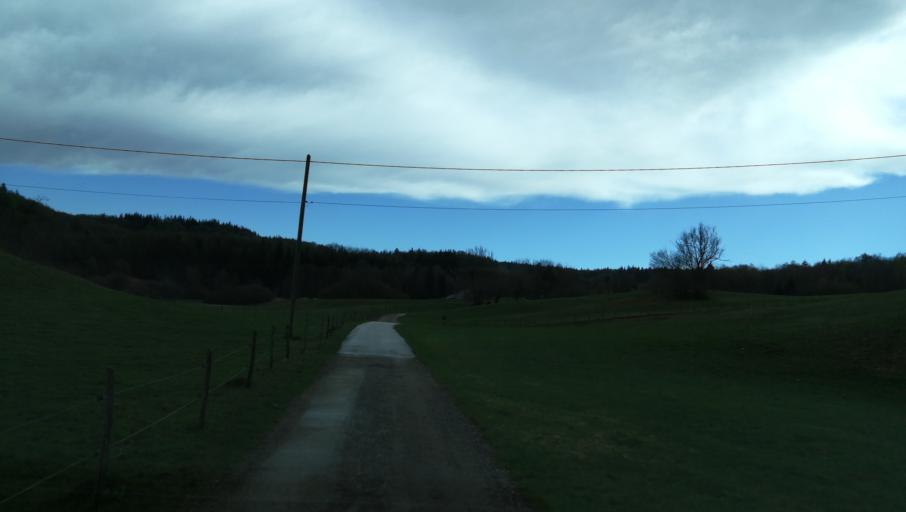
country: FR
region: Franche-Comte
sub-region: Departement du Jura
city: Lavans-les-Saint-Claude
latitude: 46.3195
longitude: 5.8090
